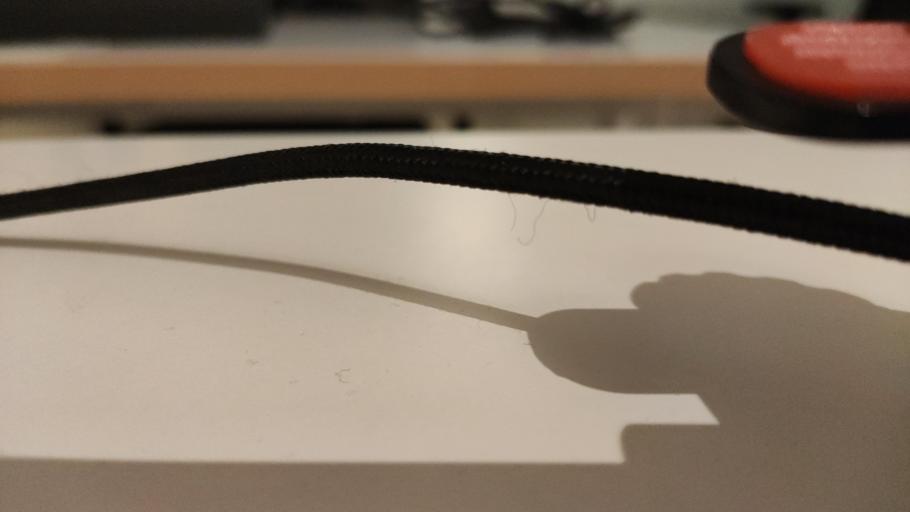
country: RU
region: Moskovskaya
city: Bogorodskoye
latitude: 56.4404
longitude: 37.9043
